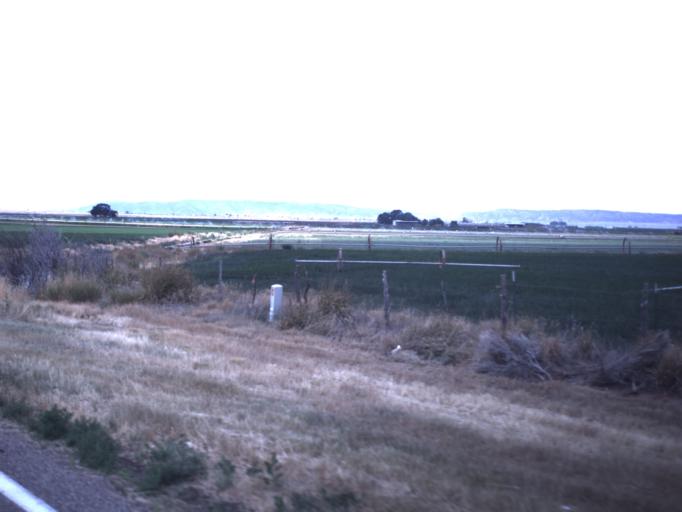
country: US
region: Utah
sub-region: Iron County
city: Parowan
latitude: 37.8784
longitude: -112.7814
